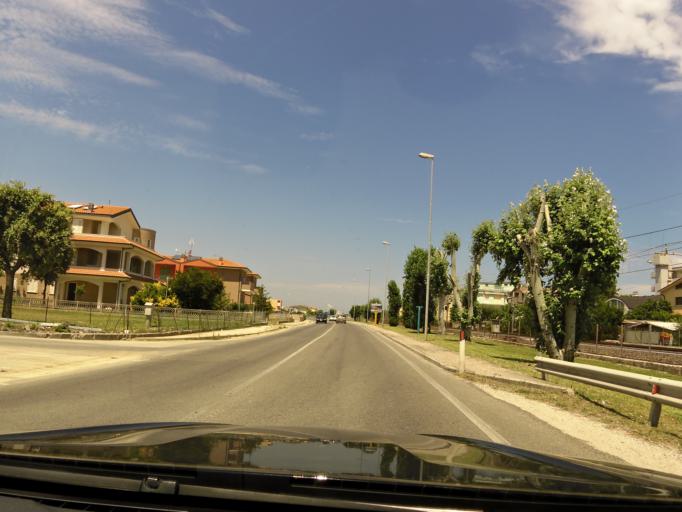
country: IT
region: The Marches
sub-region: Provincia di Pesaro e Urbino
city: Marotta
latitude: 43.7760
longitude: 13.1267
